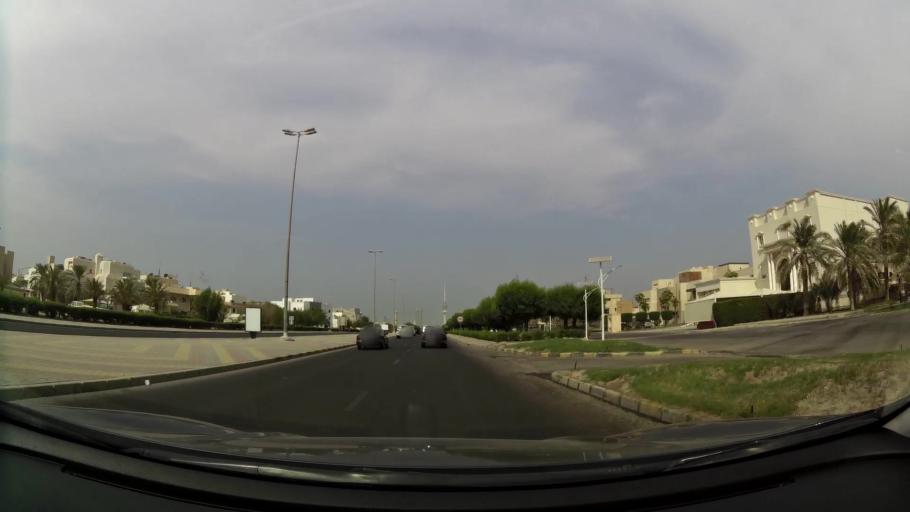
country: KW
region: Al Asimah
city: Ash Shamiyah
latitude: 29.3404
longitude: 47.9853
